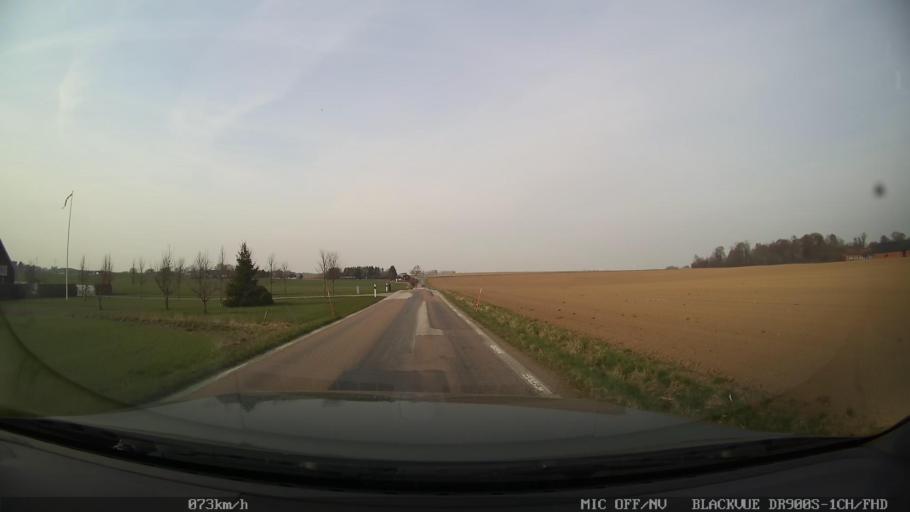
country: SE
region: Skane
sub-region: Ystads Kommun
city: Ystad
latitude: 55.4508
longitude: 13.8312
